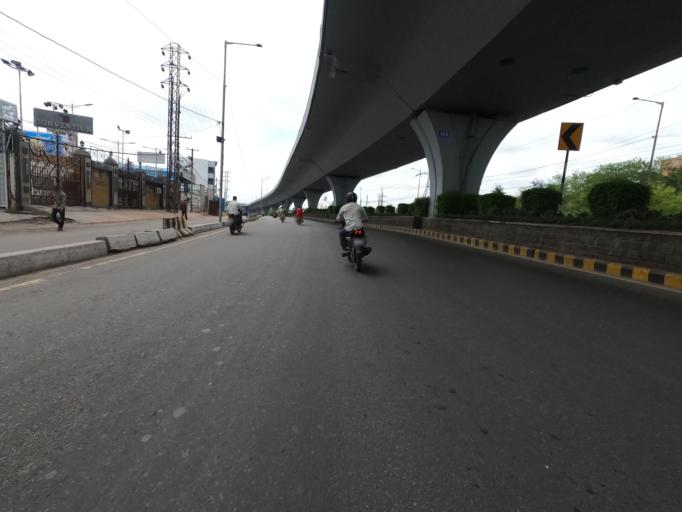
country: IN
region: Telangana
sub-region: Hyderabad
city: Hyderabad
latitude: 17.3434
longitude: 78.4178
